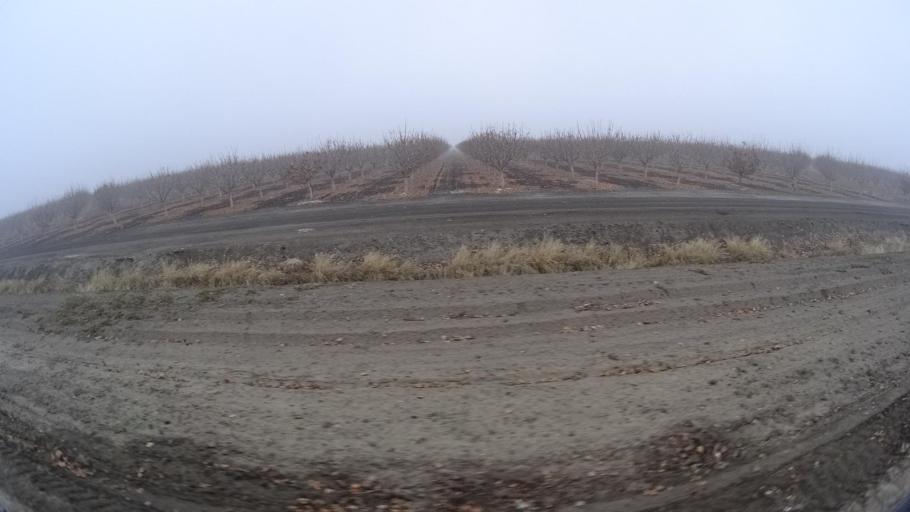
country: US
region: California
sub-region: Kern County
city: Buttonwillow
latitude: 35.4562
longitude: -119.5544
